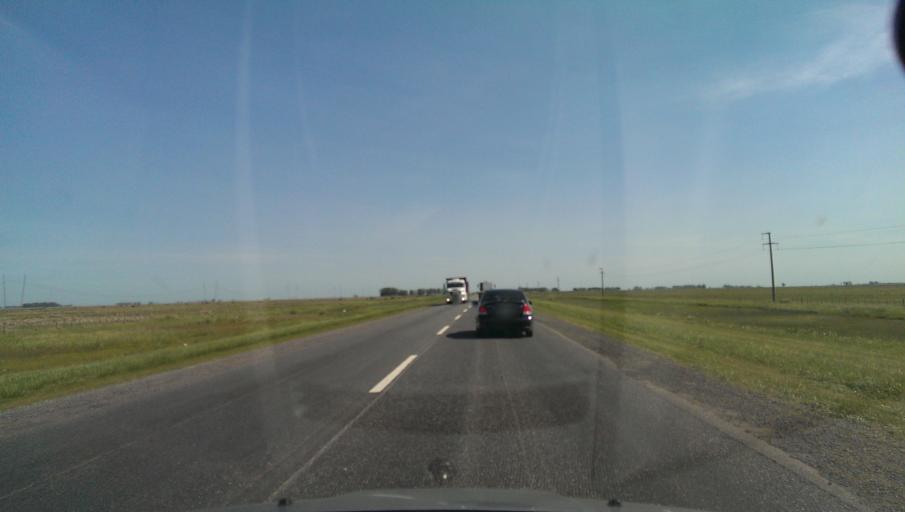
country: AR
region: Buenos Aires
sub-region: Partido de Azul
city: Azul
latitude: -36.5900
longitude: -59.6530
